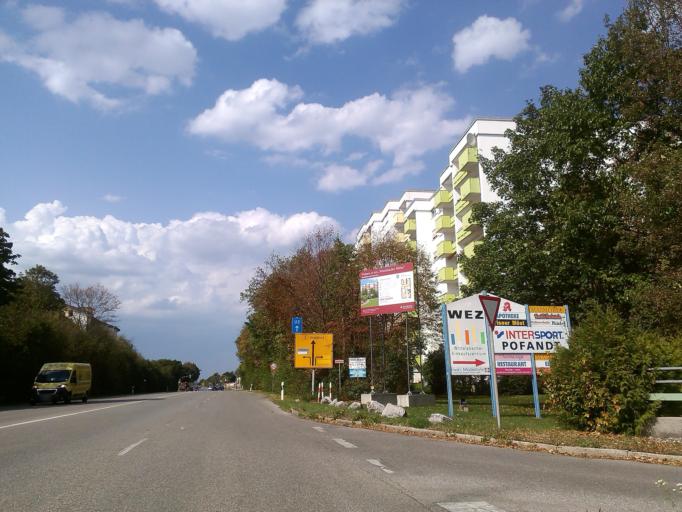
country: DE
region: Bavaria
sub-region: Upper Bavaria
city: Germering
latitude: 48.1352
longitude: 11.3742
